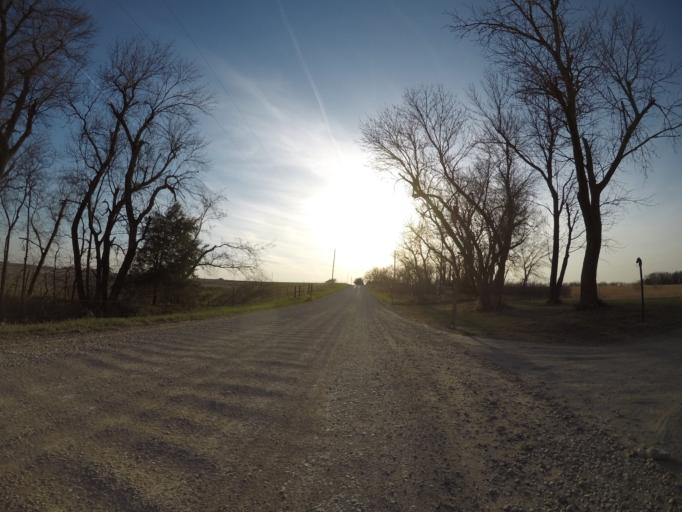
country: US
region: Kansas
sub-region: Riley County
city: Manhattan
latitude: 39.2545
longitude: -96.6779
